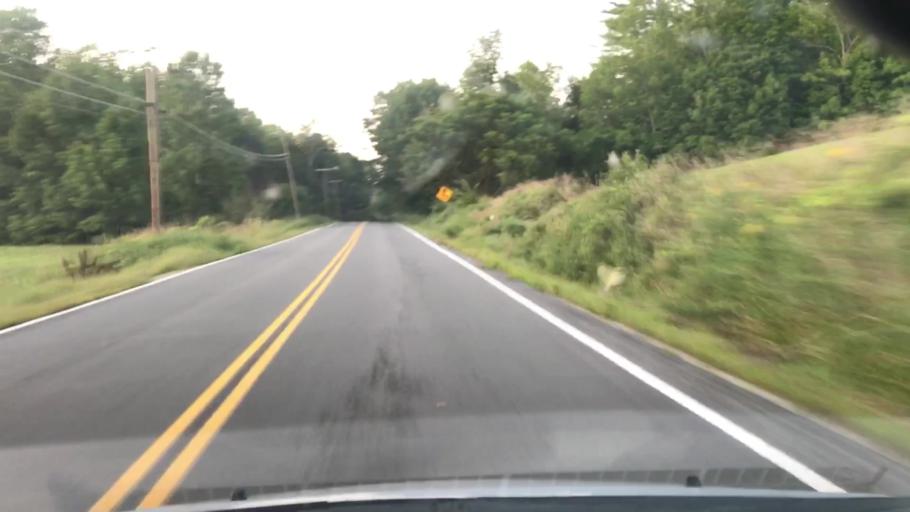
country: US
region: New Hampshire
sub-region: Grafton County
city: Woodsville
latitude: 44.2281
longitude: -72.0463
